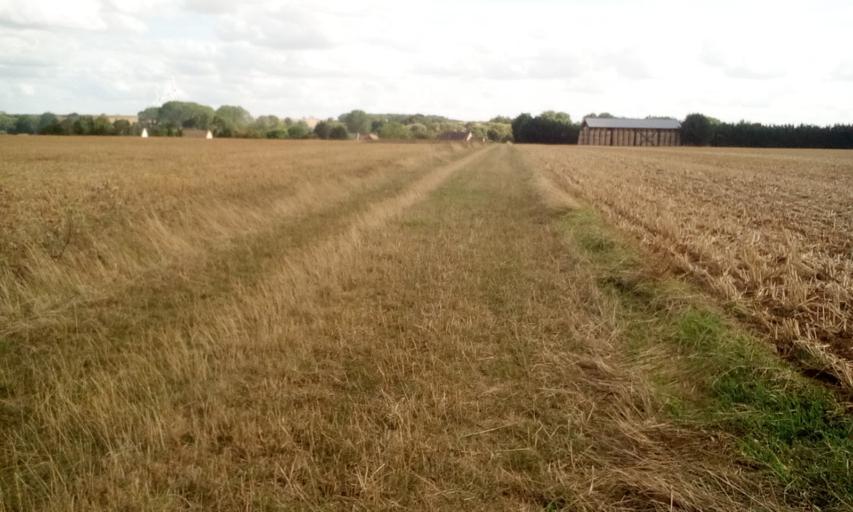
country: FR
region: Lower Normandy
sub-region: Departement du Calvados
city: Saint-Sylvain
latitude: 49.0756
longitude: -0.1967
